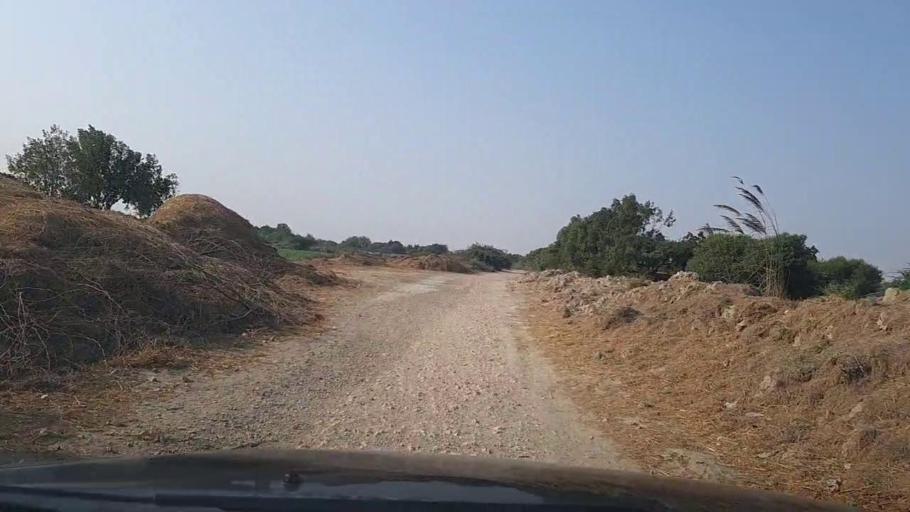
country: PK
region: Sindh
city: Mirpur Sakro
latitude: 24.6365
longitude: 67.7515
